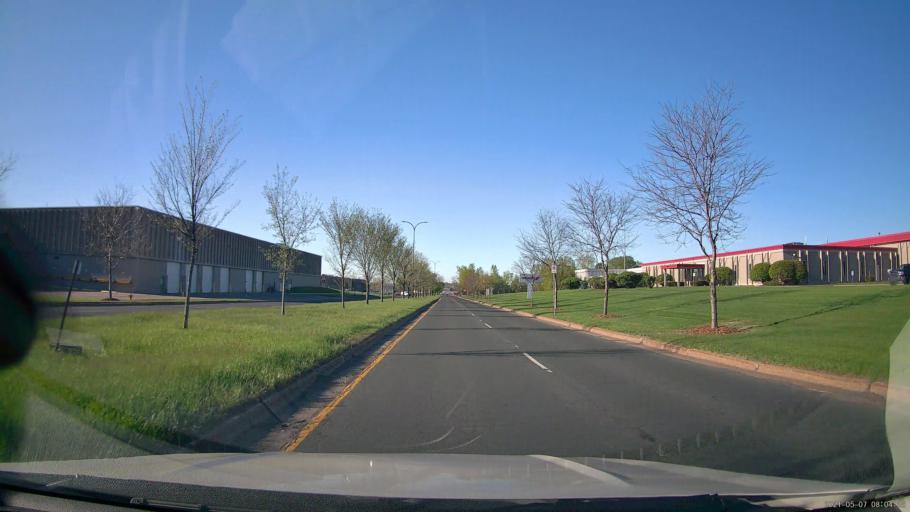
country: US
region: Minnesota
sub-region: Ramsey County
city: Lauderdale
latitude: 44.9983
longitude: -93.2117
